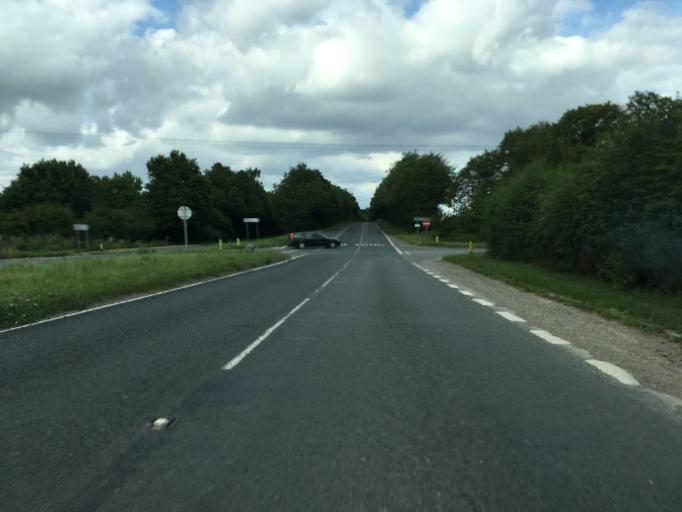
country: GB
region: England
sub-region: Hampshire
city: Kings Worthy
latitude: 51.1240
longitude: -1.2658
